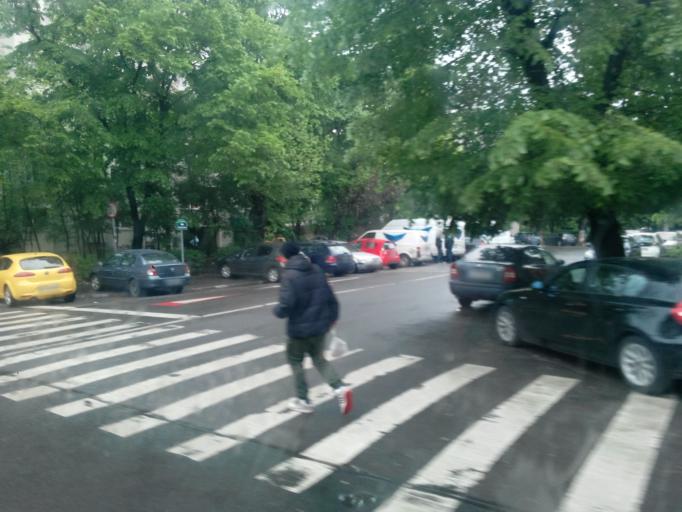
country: RO
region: Ilfov
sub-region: Comuna Fundeni-Dobroesti
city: Fundeni
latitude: 44.4467
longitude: 26.1359
